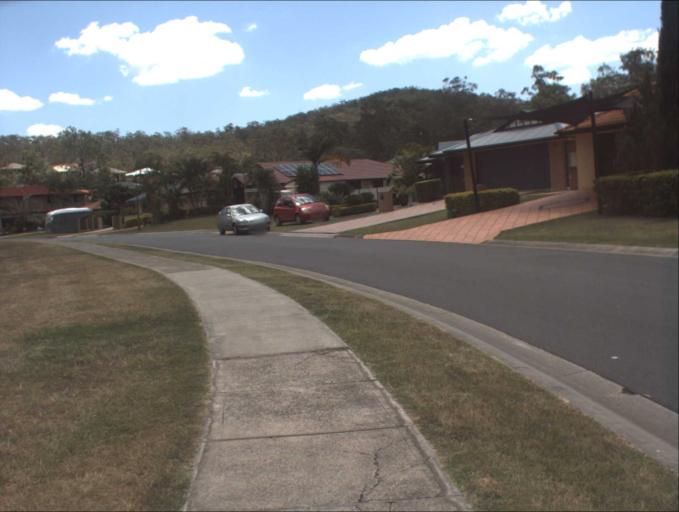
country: AU
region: Queensland
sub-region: Logan
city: Windaroo
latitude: -27.7371
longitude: 153.1893
